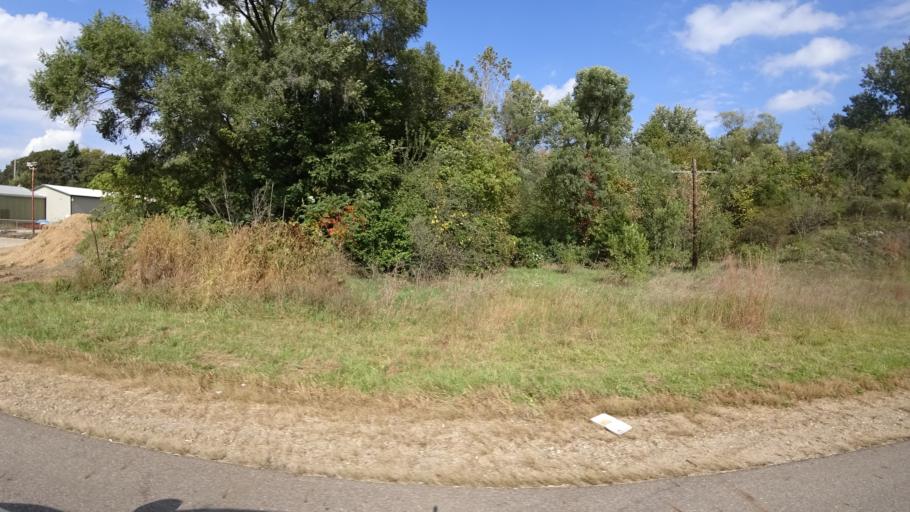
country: US
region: Michigan
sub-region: Saint Joseph County
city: Three Rivers
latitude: 41.9256
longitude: -85.6231
